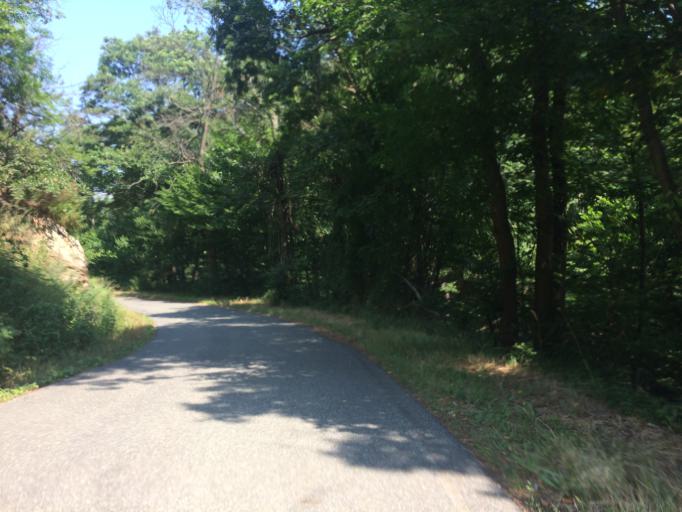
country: IT
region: Piedmont
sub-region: Provincia di Alessandria
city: Malvicino
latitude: 44.5389
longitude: 8.4104
